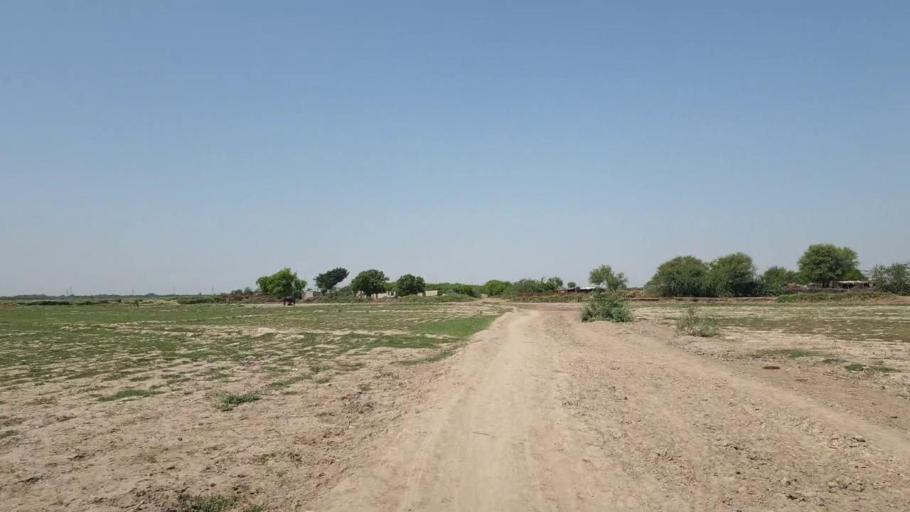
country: PK
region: Sindh
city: Hyderabad
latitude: 25.4680
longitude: 68.4233
